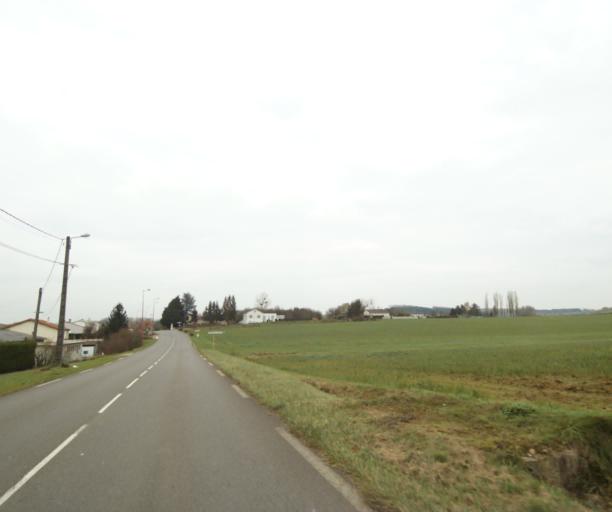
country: FR
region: Lorraine
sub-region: Departement de Meurthe-et-Moselle
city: Mancieulles
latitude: 49.2908
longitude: 5.8882
